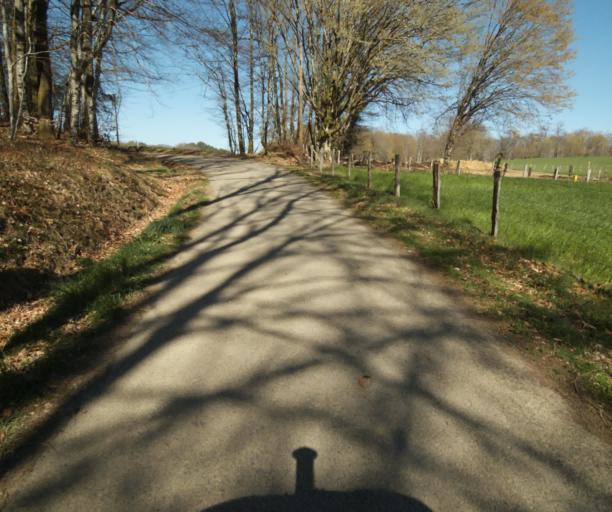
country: FR
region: Limousin
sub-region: Departement de la Correze
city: Chameyrat
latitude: 45.2515
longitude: 1.7069
